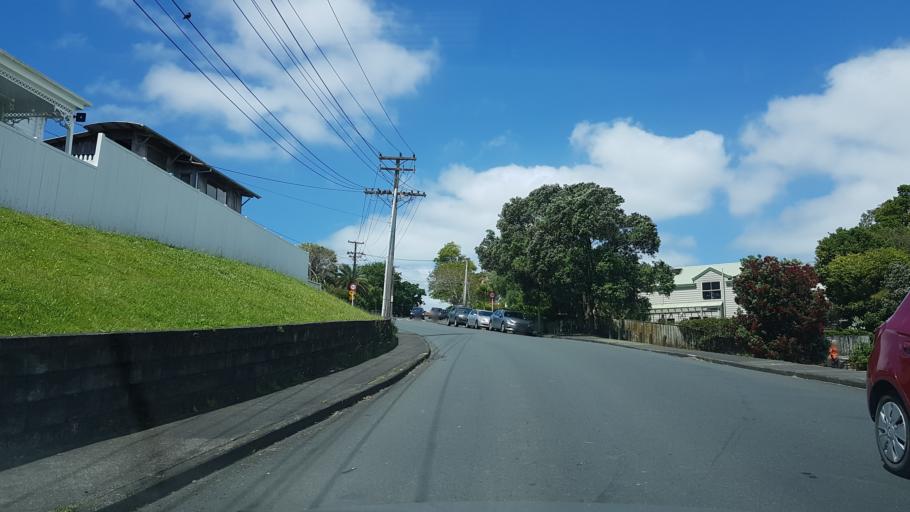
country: NZ
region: Auckland
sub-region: Auckland
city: North Shore
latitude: -36.8153
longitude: 174.7416
